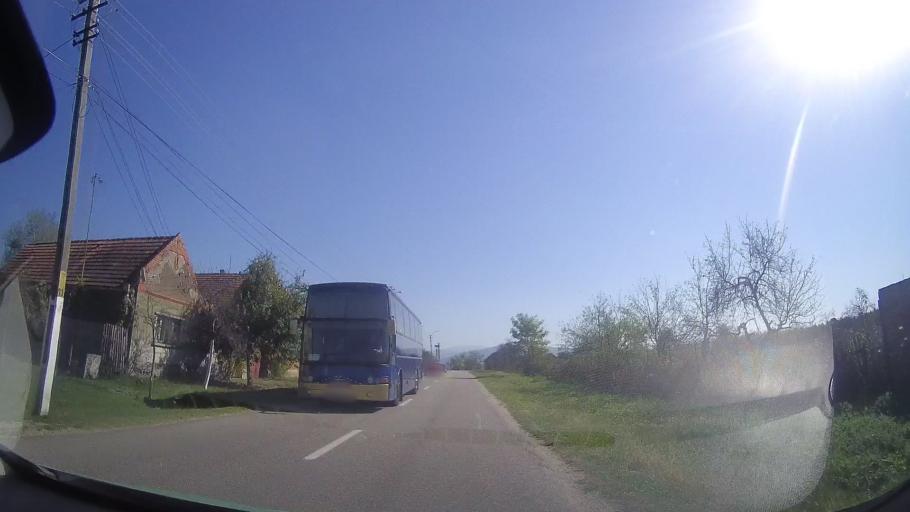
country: RO
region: Timis
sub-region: Comuna Traian Vuia
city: Traian Vuia
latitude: 45.7881
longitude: 22.0317
